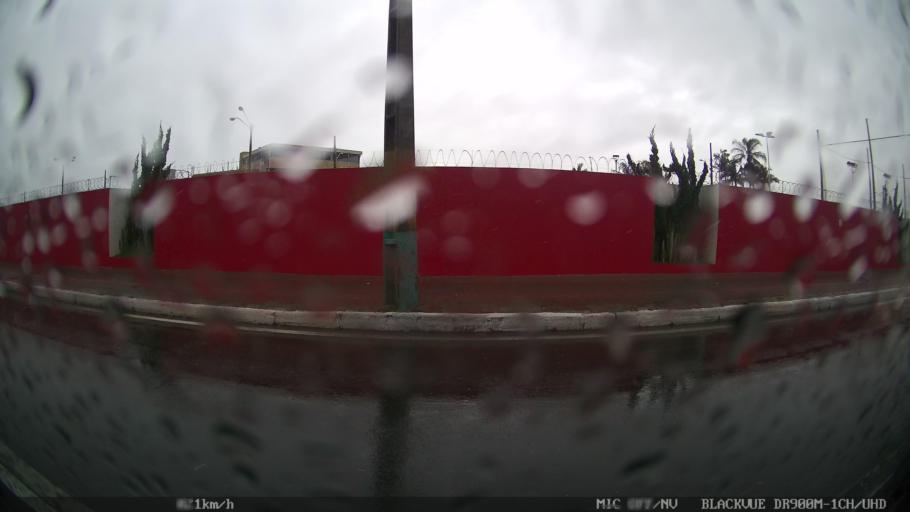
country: BR
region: Santa Catarina
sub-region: Navegantes
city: Navegantes
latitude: -26.8839
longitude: -48.6526
